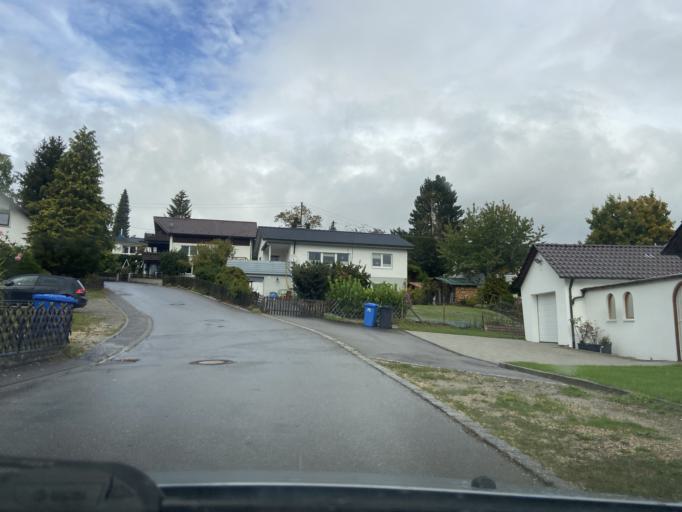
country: DE
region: Baden-Wuerttemberg
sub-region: Tuebingen Region
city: Bingen
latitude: 48.1116
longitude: 9.2650
